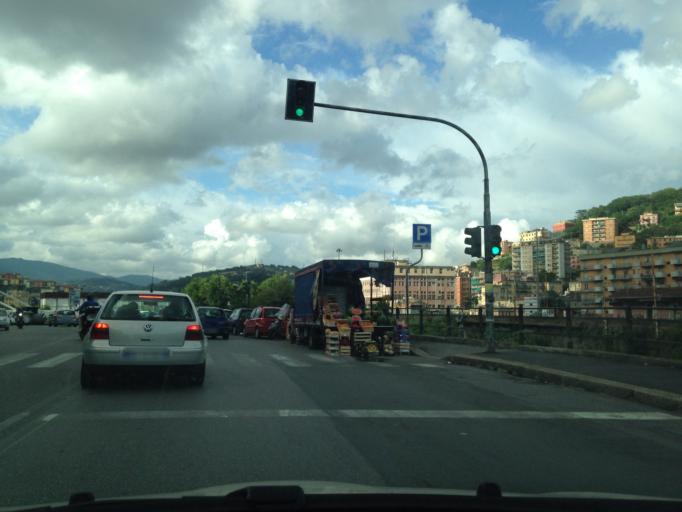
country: IT
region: Liguria
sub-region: Provincia di Genova
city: Manesseno
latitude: 44.4587
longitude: 8.8989
